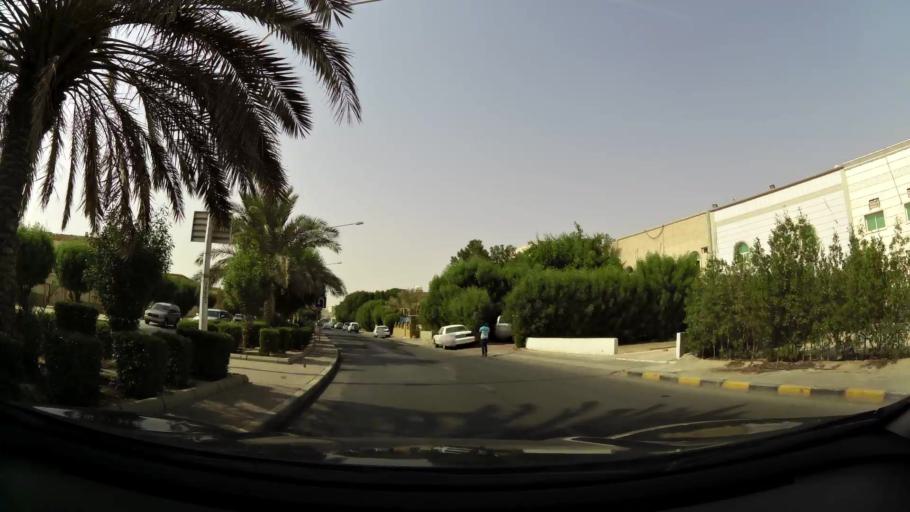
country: KW
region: Muhafazat al Jahra'
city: Al Jahra'
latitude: 29.3320
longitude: 47.6573
